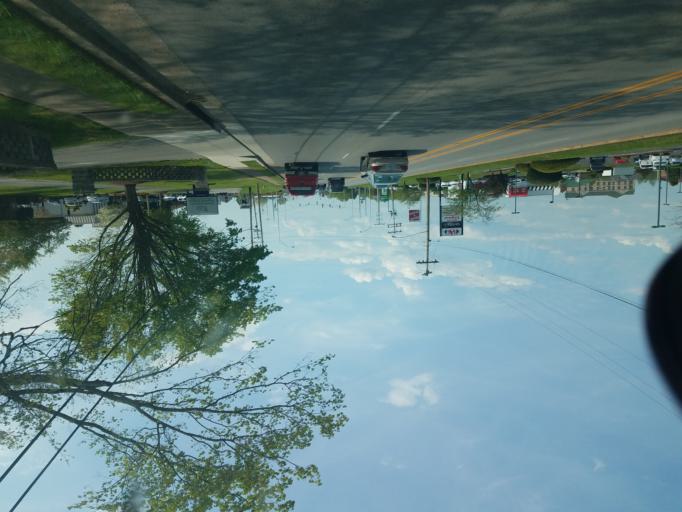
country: US
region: Kentucky
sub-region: Warren County
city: Bowling Green
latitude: 36.9715
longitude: -86.4349
